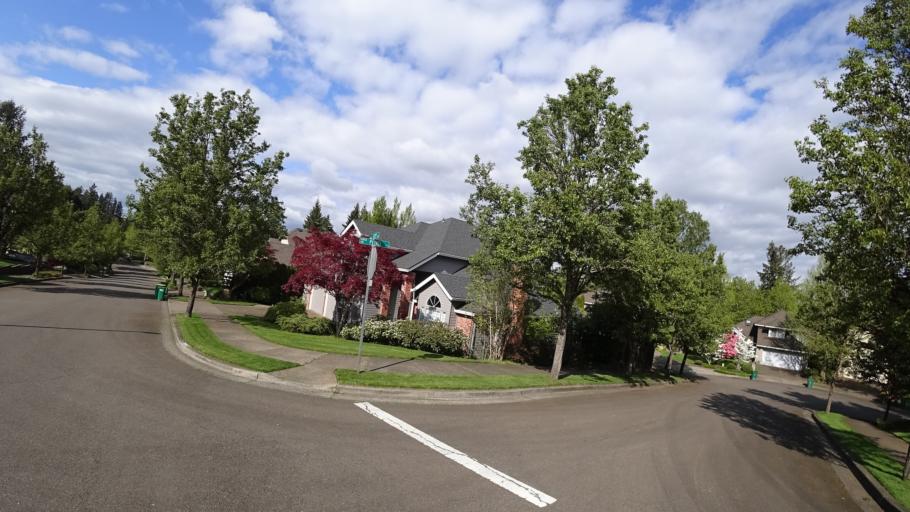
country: US
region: Oregon
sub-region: Washington County
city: Beaverton
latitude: 45.4450
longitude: -122.8343
